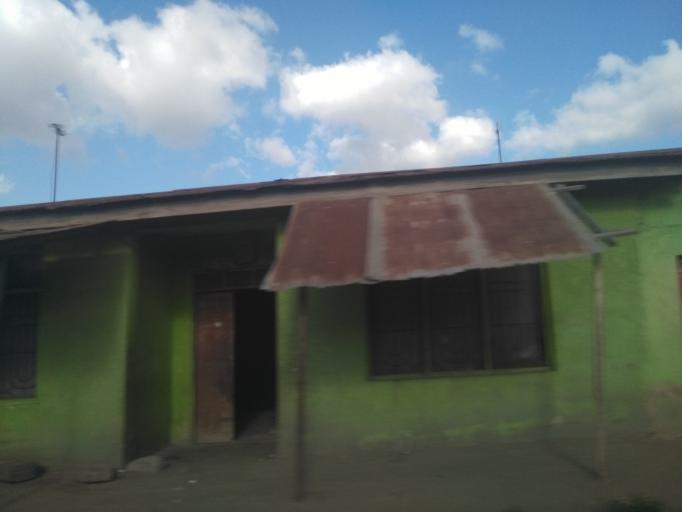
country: TZ
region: Dar es Salaam
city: Dar es Salaam
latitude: -6.8648
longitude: 39.2598
